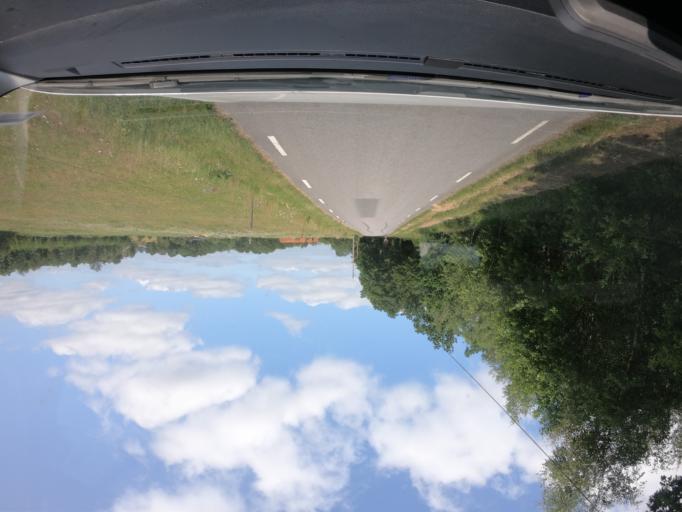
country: SE
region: Skane
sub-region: Hassleholms Kommun
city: Sosdala
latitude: 56.0322
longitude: 13.6449
